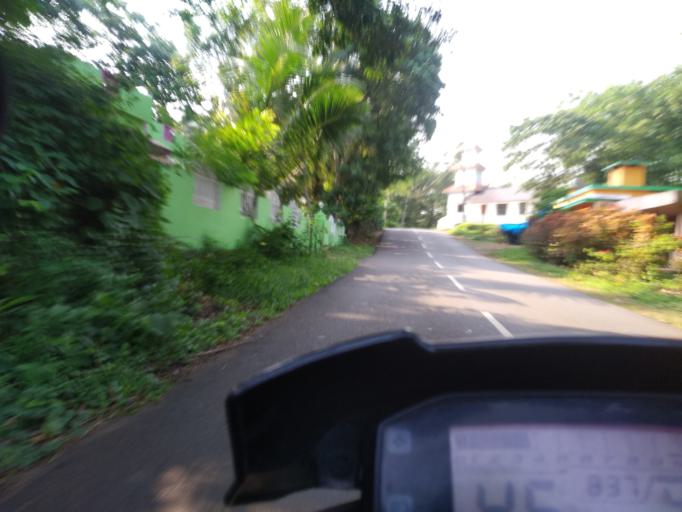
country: IN
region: Kerala
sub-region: Ernakulam
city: Ramamangalam
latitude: 9.9129
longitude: 76.4361
